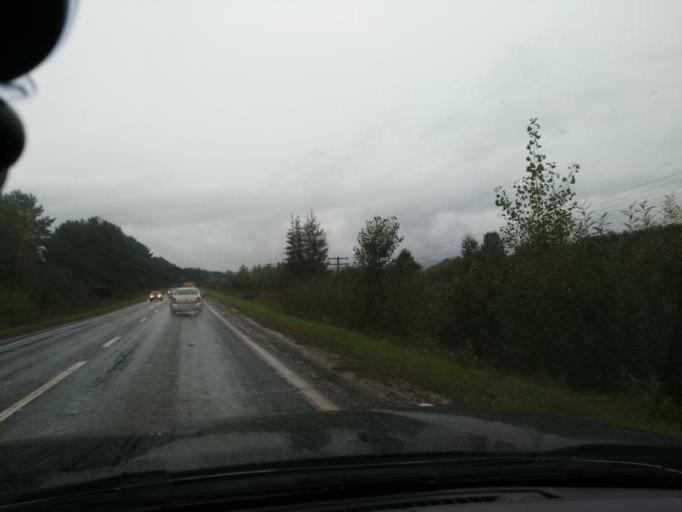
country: RU
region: Perm
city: Yugo-Kamskiy
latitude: 57.6819
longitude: 55.5729
